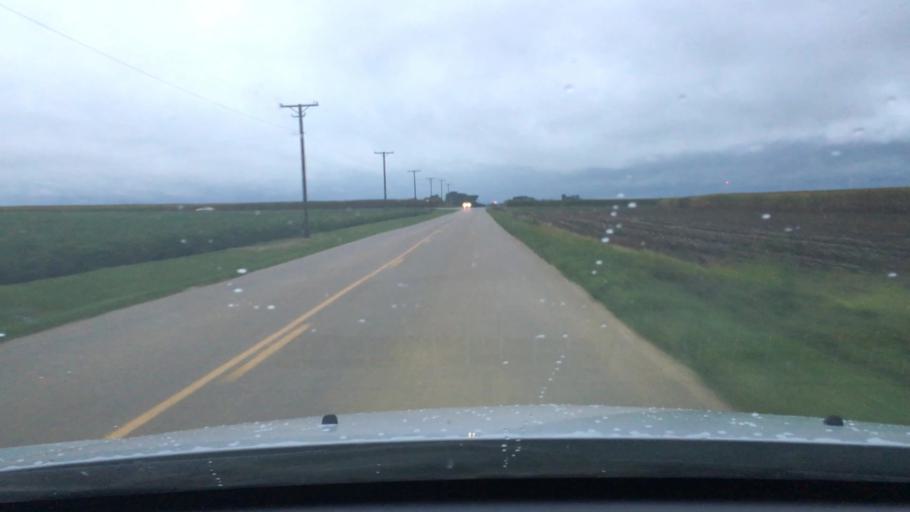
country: US
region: Illinois
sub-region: DeKalb County
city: Malta
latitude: 41.8501
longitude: -88.9612
